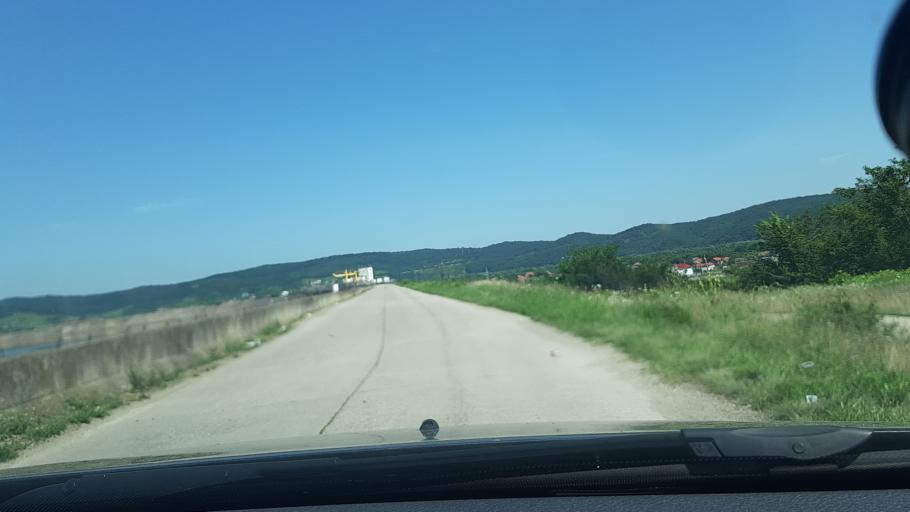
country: RO
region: Hunedoara
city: Bucium-Orlea
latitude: 45.5888
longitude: 22.9603
